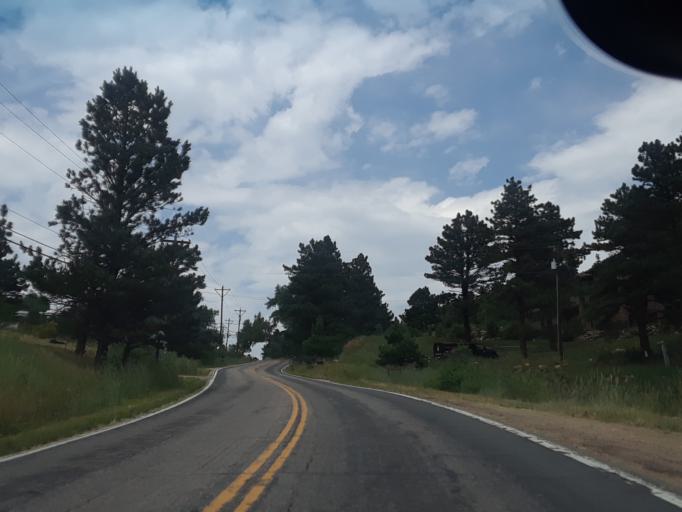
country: US
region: Colorado
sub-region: Boulder County
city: Boulder
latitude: 40.0712
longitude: -105.3015
